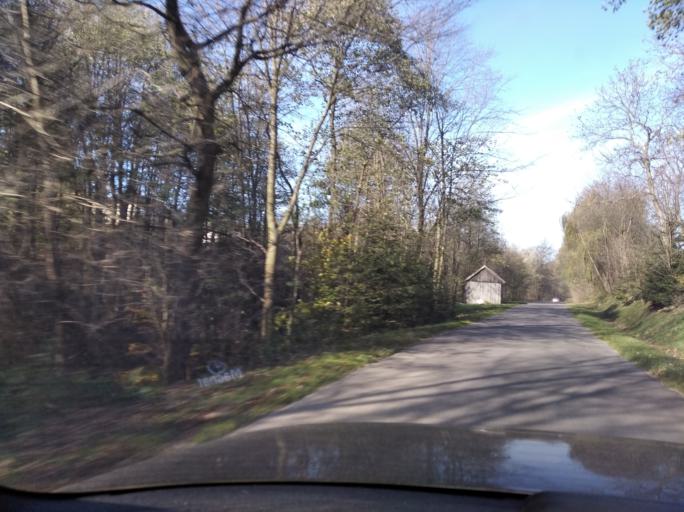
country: PL
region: Subcarpathian Voivodeship
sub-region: Powiat ropczycko-sedziszowski
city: Wielopole Skrzynskie
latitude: 49.9021
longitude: 21.5699
